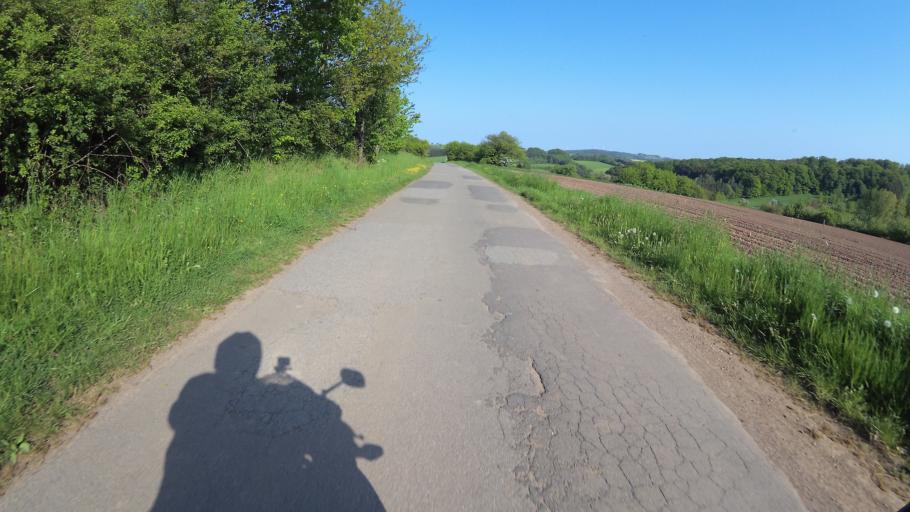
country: DE
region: Saarland
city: Marpingen
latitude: 49.4267
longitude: 7.0661
